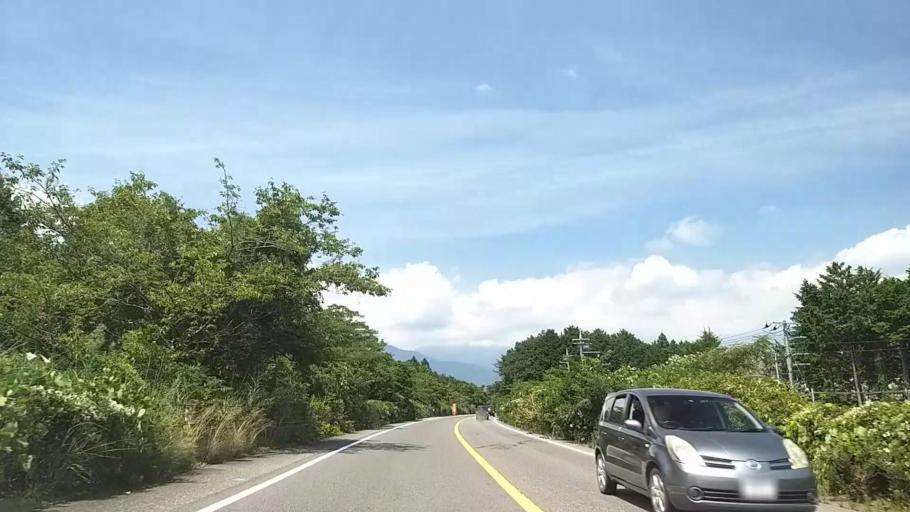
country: JP
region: Shizuoka
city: Fujinomiya
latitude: 35.3184
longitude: 138.5915
